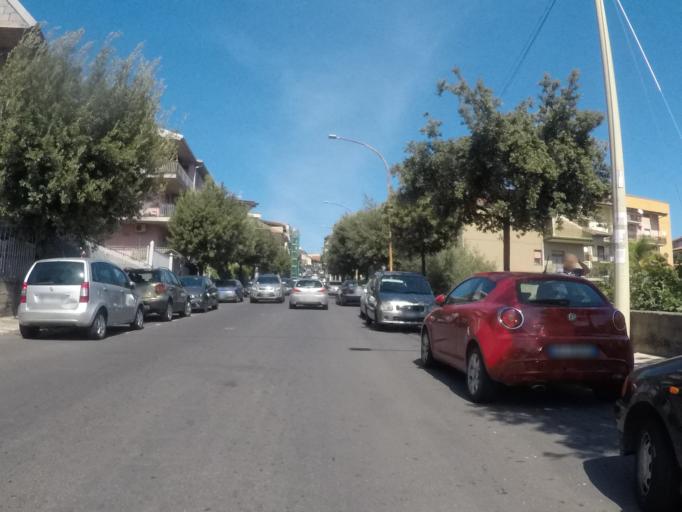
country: IT
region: Sicily
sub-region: Catania
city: Motta Sant'Anastasia
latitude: 37.5131
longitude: 14.9663
